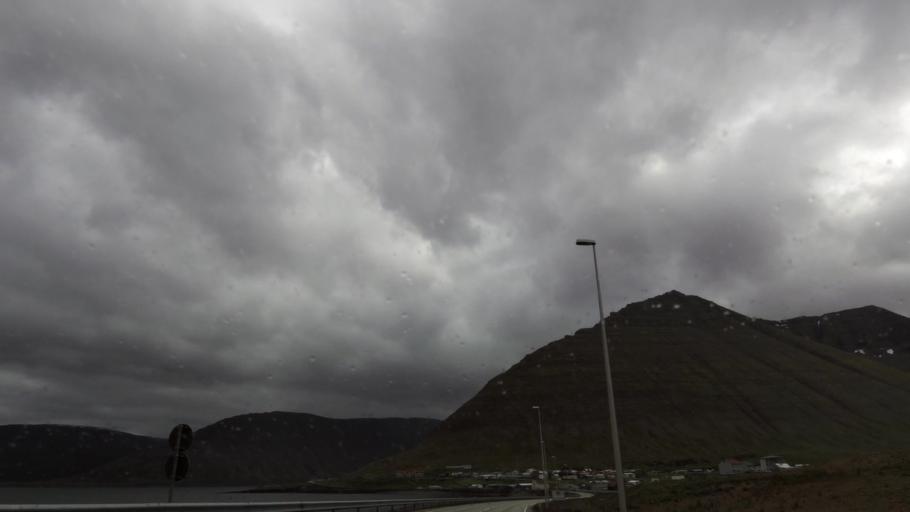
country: IS
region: Westfjords
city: Isafjoerdur
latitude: 66.1165
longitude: -23.1208
